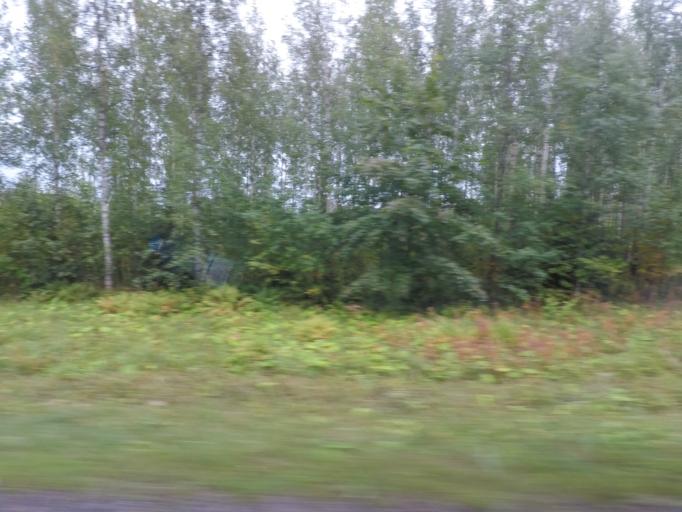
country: FI
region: Southern Savonia
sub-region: Pieksaemaeki
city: Joroinen
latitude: 62.1212
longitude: 27.8391
